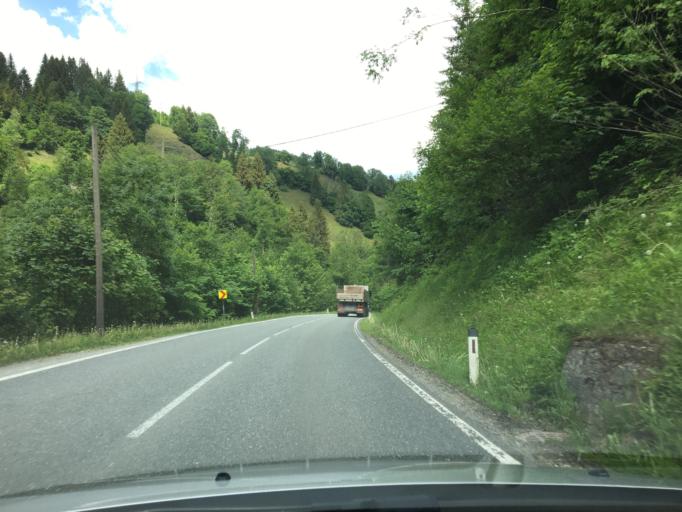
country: AT
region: Salzburg
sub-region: Politischer Bezirk Sankt Johann im Pongau
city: Wagrain
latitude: 47.3352
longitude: 13.2641
